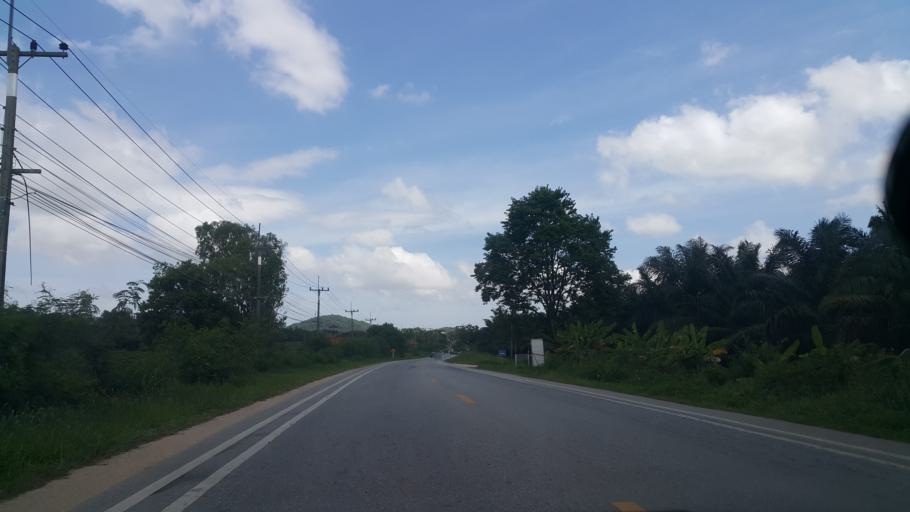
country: TH
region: Rayong
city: Ban Chang
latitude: 12.8152
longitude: 101.0594
